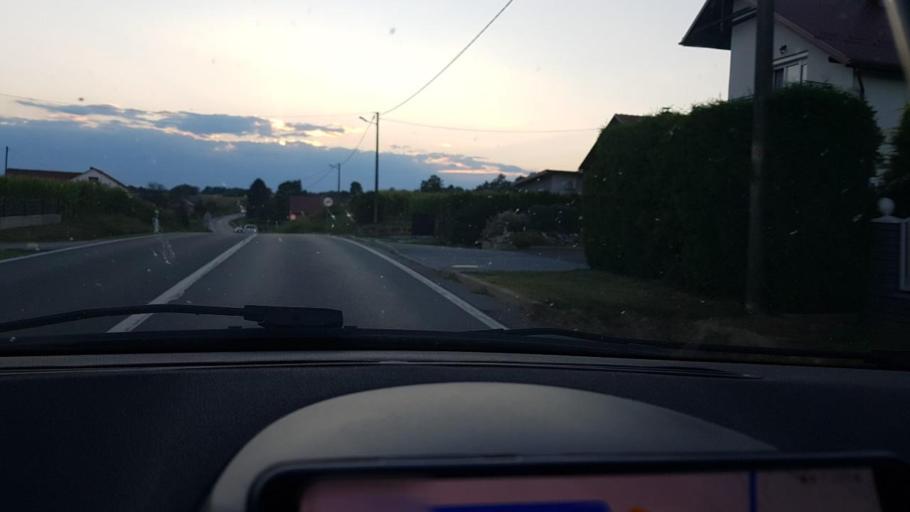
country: HR
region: Bjelovarsko-Bilogorska
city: Zdralovi
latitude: 45.8674
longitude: 16.9096
